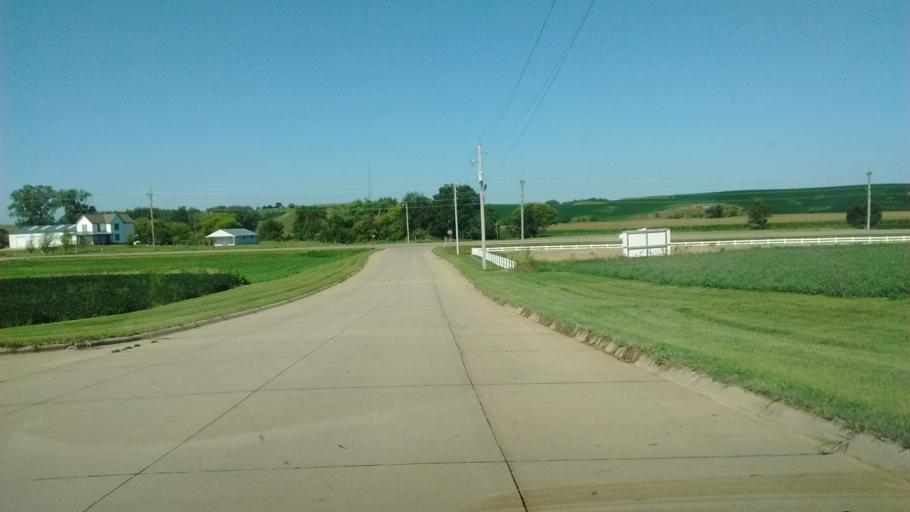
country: US
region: Iowa
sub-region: Woodbury County
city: Moville
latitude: 42.4965
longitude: -96.0701
